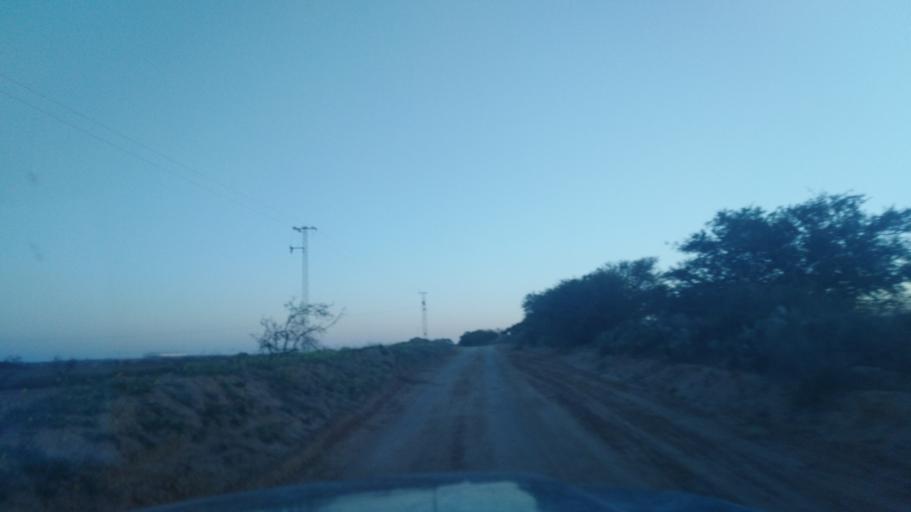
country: TN
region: Safaqis
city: Sfax
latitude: 34.7322
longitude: 10.4450
